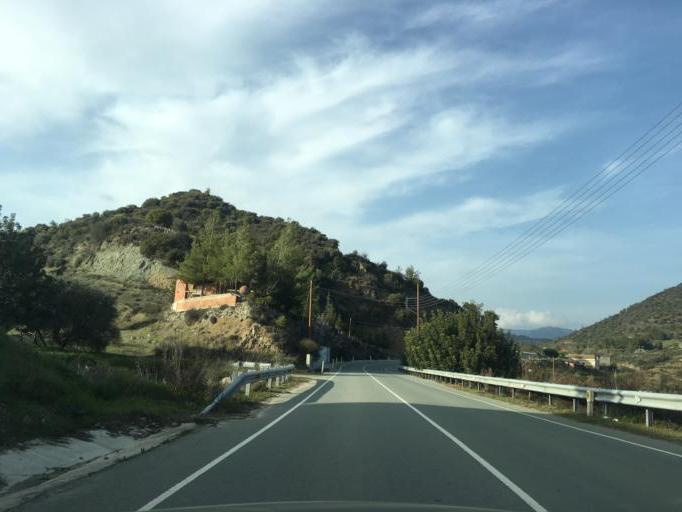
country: CY
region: Limassol
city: Pelendri
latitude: 34.8188
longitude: 32.9644
